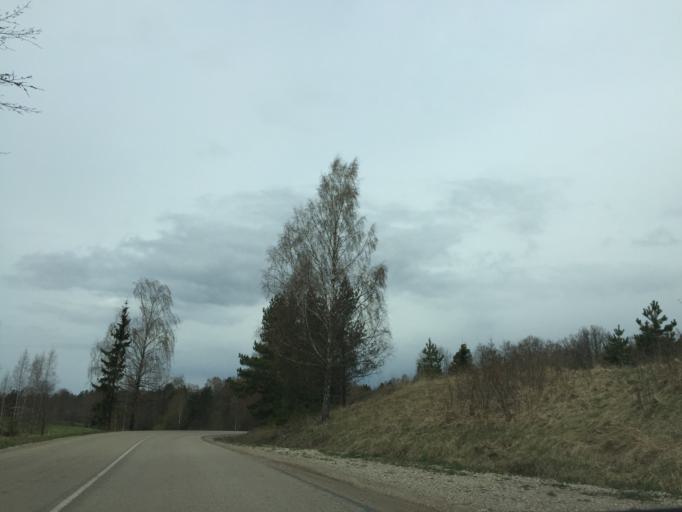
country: LV
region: Amatas Novads
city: Drabesi
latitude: 57.2588
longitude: 25.2744
